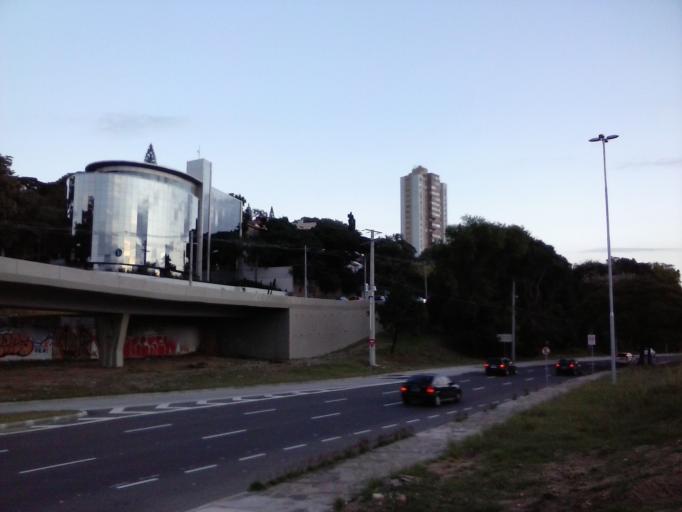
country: BR
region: Rio Grande do Sul
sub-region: Porto Alegre
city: Porto Alegre
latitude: -30.0743
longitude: -51.2422
